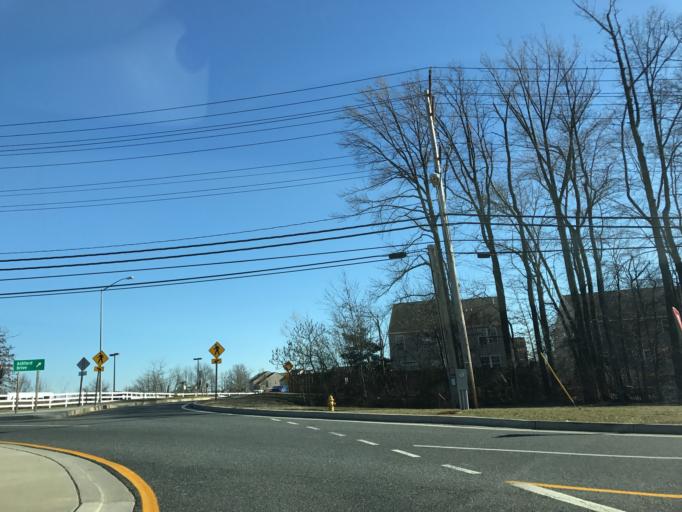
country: US
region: Maryland
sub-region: Harford County
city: Riverside
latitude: 39.4859
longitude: -76.2390
